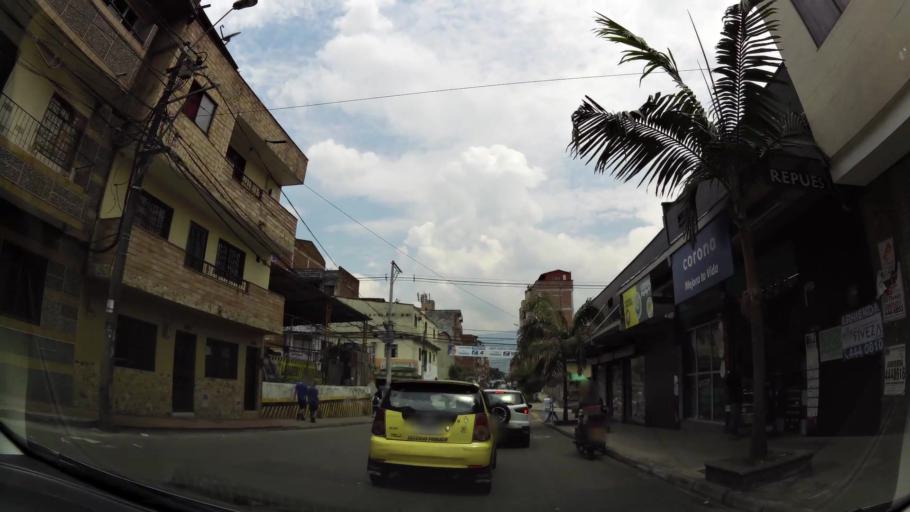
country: CO
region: Antioquia
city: Sabaneta
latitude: 6.1689
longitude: -75.6101
